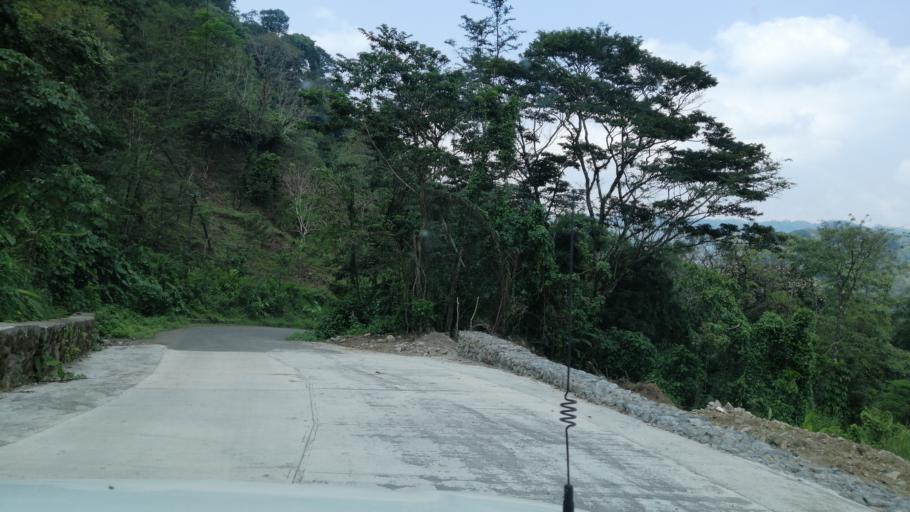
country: MX
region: Chiapas
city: Ostuacan
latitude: 17.3957
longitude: -93.3308
